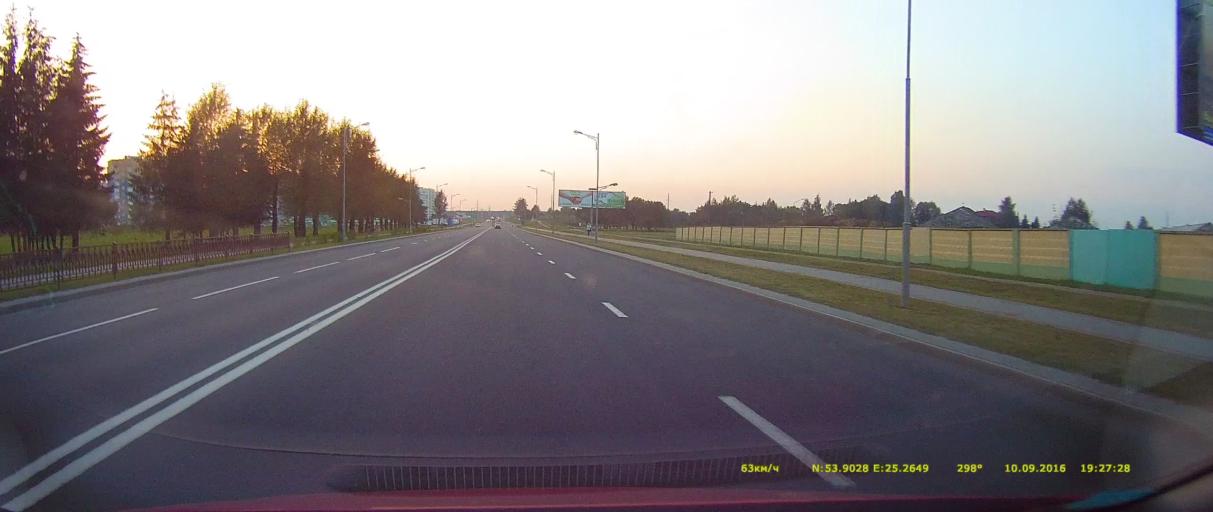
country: BY
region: Grodnenskaya
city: Lida
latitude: 53.9029
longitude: 25.2647
